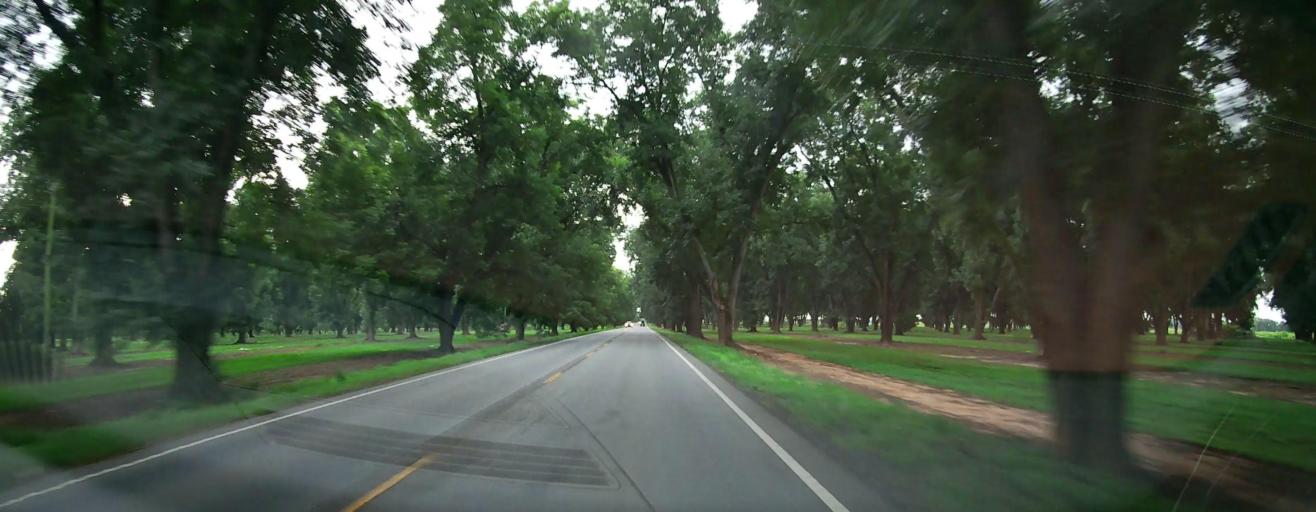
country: US
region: Georgia
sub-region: Houston County
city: Perry
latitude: 32.4388
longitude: -83.6554
